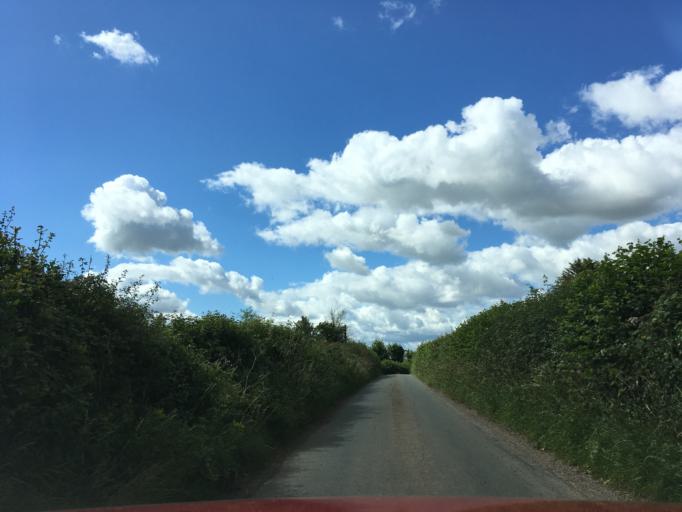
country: GB
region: England
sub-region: Gloucestershire
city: Newent
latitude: 51.8463
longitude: -2.3964
